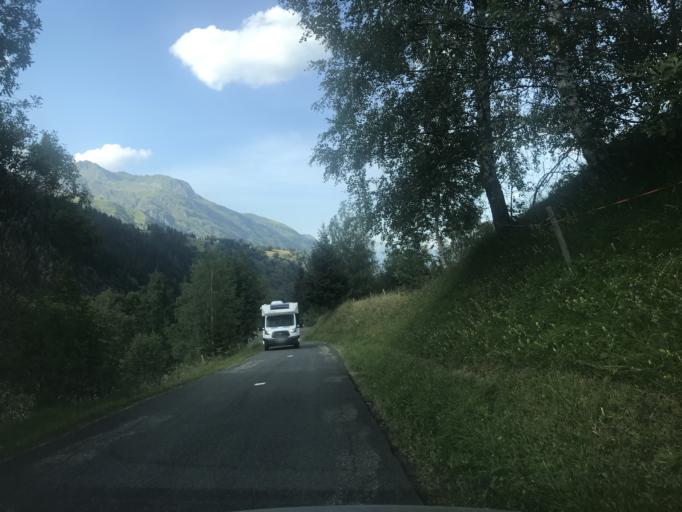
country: FR
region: Rhone-Alpes
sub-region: Departement de la Savoie
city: Saint-Etienne-de-Cuines
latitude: 45.2647
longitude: 6.1968
